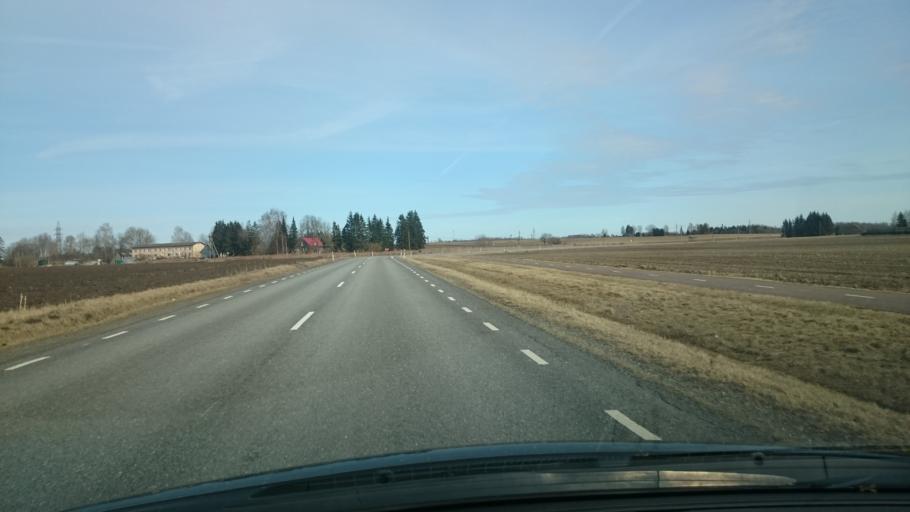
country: EE
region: Jaervamaa
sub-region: Paide linn
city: Paide
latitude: 58.8906
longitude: 25.4961
